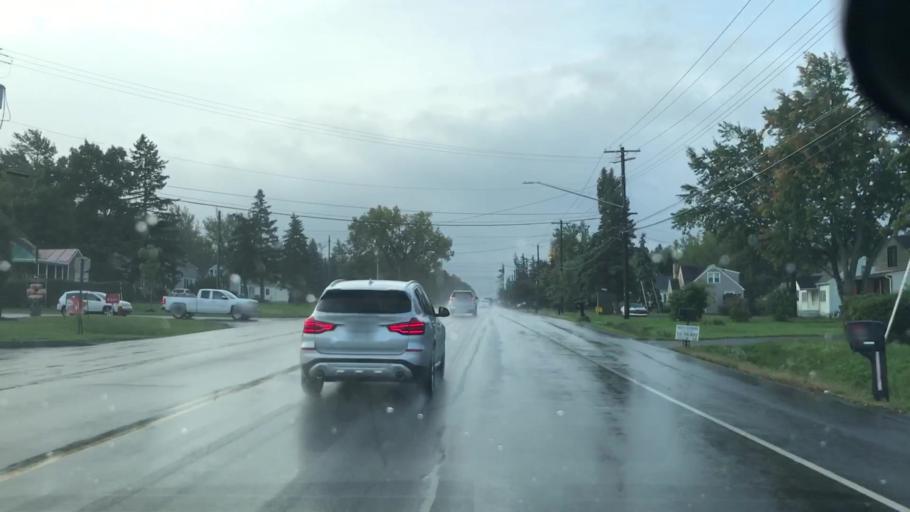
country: US
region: New York
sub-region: Erie County
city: Elma Center
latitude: 42.8257
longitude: -78.6970
